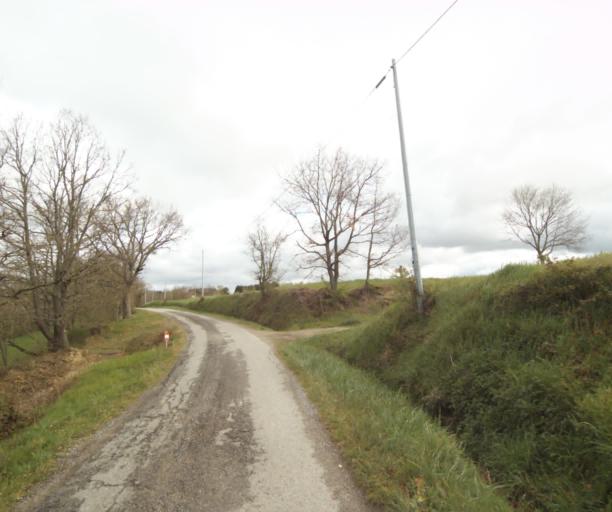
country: FR
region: Midi-Pyrenees
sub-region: Departement de l'Ariege
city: Saverdun
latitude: 43.2212
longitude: 1.5596
